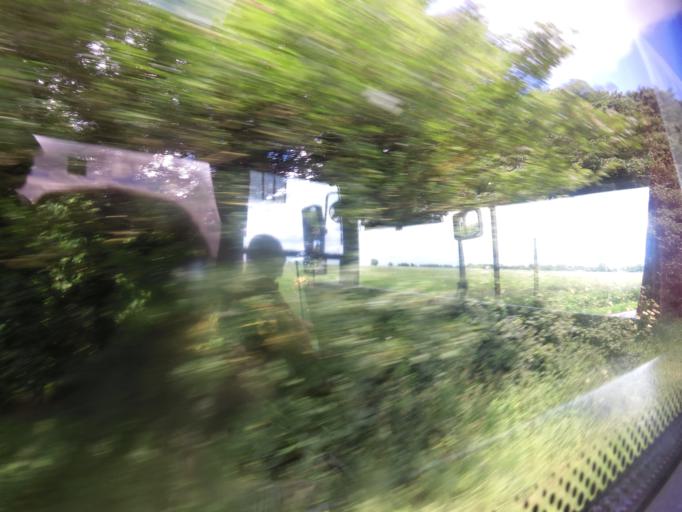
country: GB
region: England
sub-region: Norfolk
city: Aylsham
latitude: 52.8415
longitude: 1.2744
